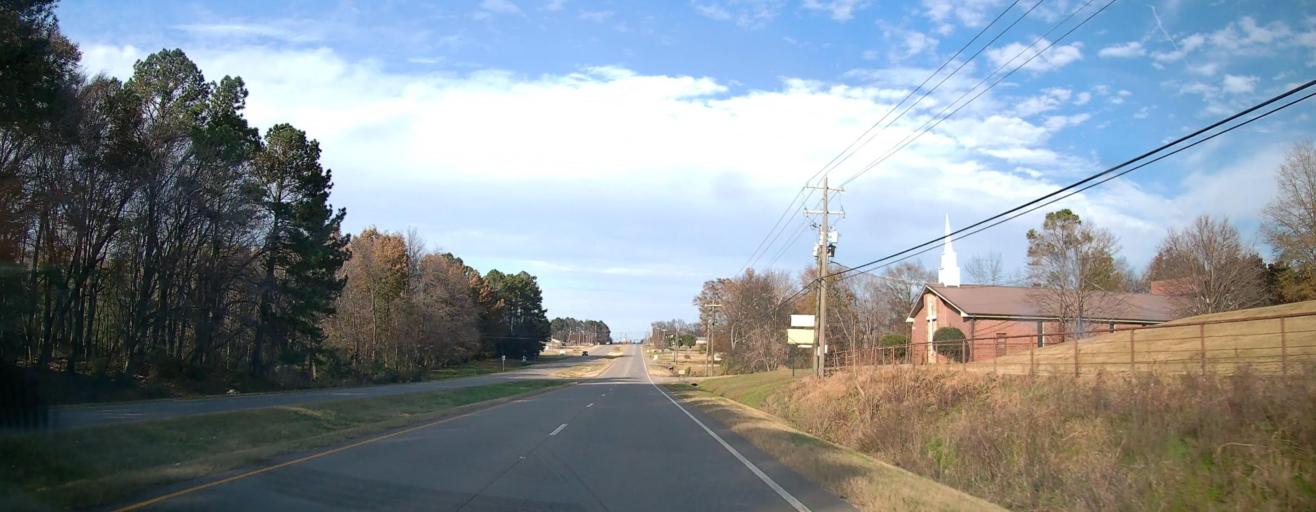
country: US
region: Alabama
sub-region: Limestone County
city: Athens
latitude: 34.7689
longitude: -86.9572
